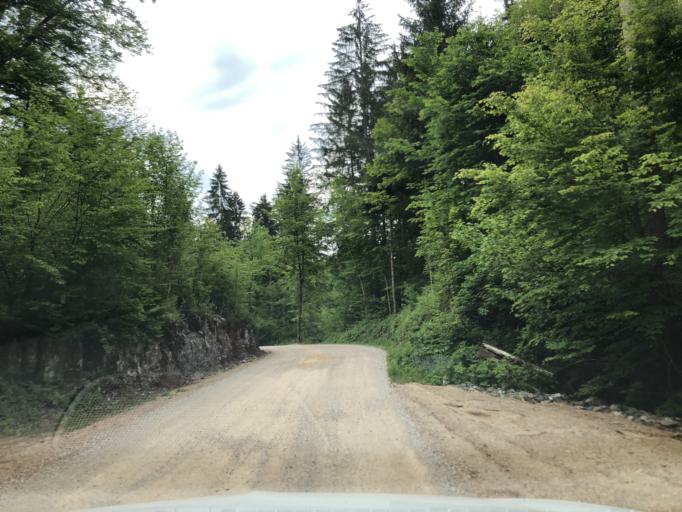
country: SI
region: Bloke
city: Nova Vas
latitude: 45.7506
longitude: 14.4640
